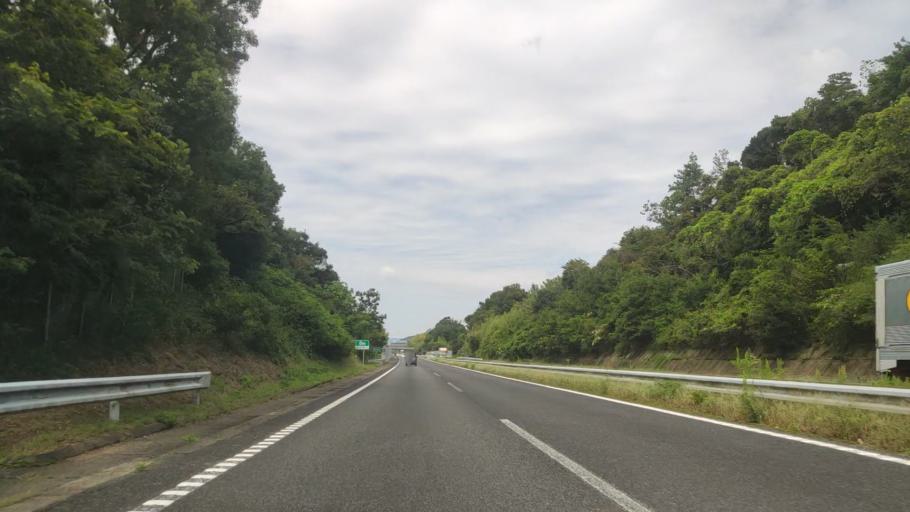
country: JP
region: Wakayama
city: Kainan
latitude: 34.1932
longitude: 135.2371
